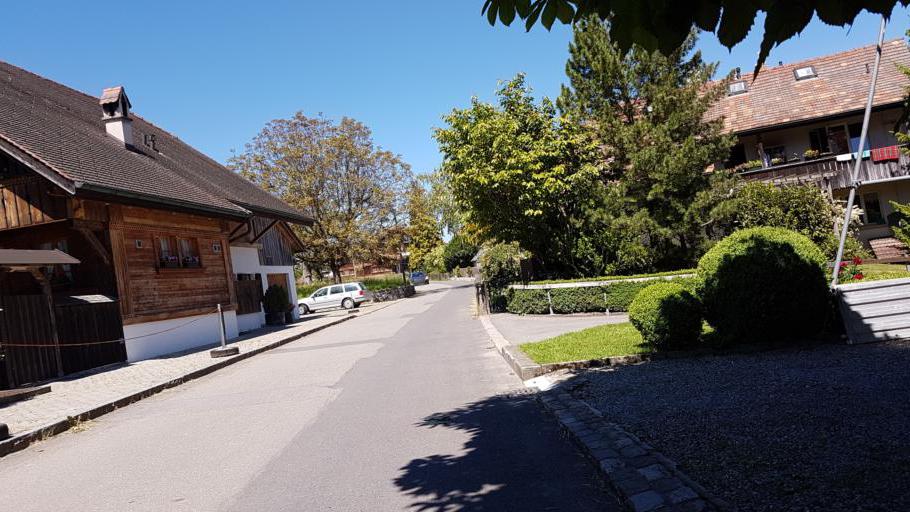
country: CH
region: Bern
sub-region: Thun District
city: Thierachern
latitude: 46.7282
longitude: 7.5775
